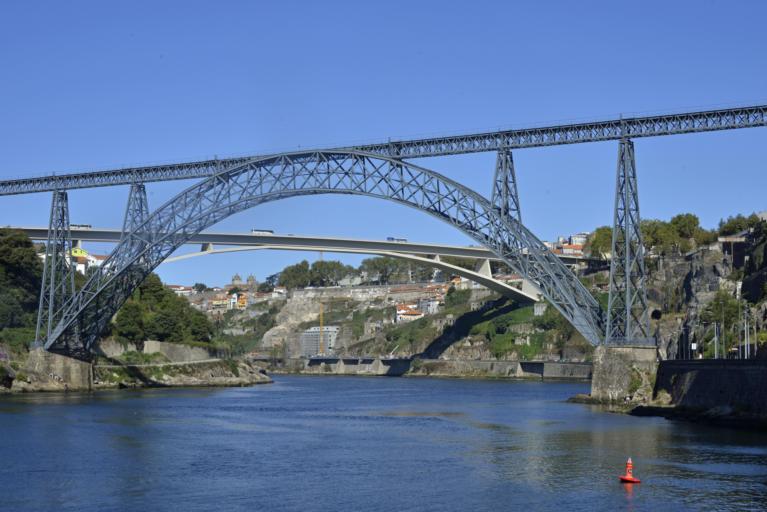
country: PT
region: Porto
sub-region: Vila Nova de Gaia
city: Oliveira do Douro
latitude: 41.1389
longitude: -8.5933
